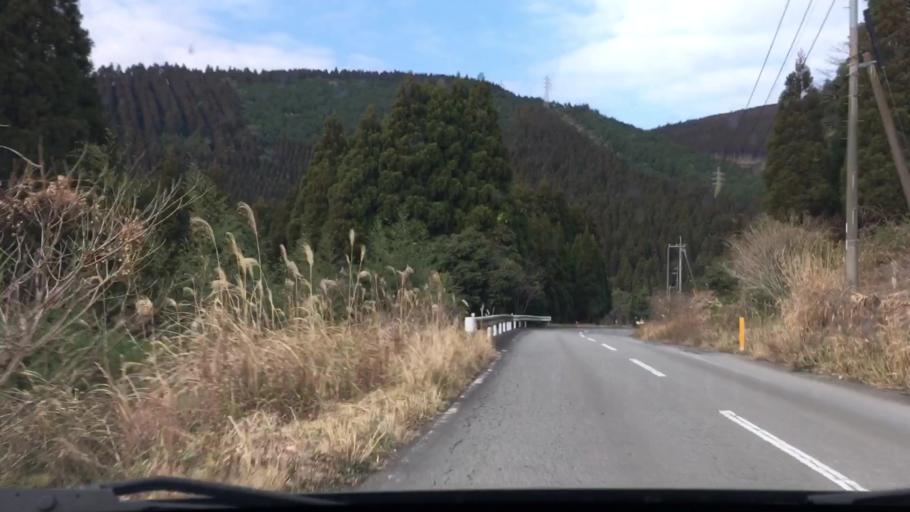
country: JP
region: Miyazaki
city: Nichinan
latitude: 31.6604
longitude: 131.3248
